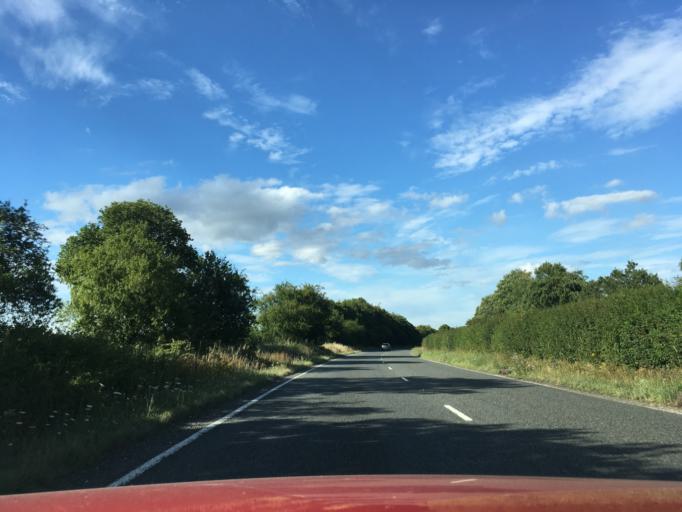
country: GB
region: England
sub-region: Hampshire
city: Romsey
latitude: 50.9724
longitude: -1.5214
